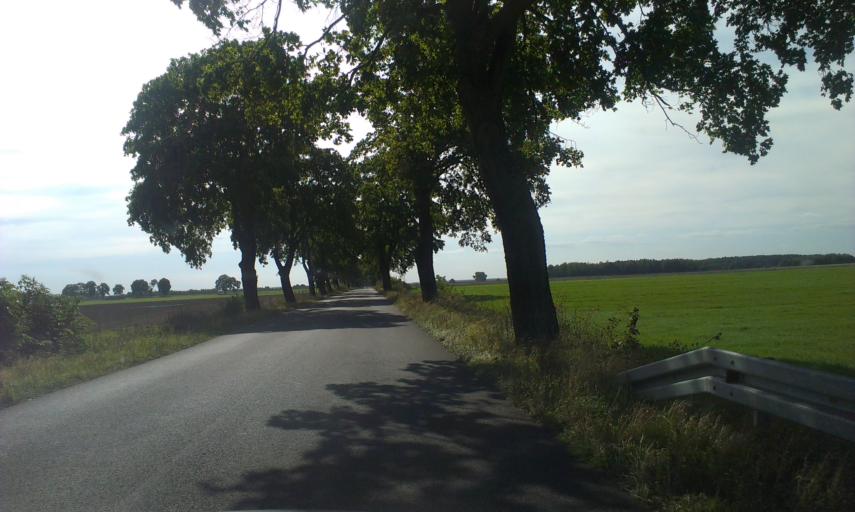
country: PL
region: Greater Poland Voivodeship
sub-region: Powiat zlotowski
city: Zlotow
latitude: 53.4740
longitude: 16.9907
